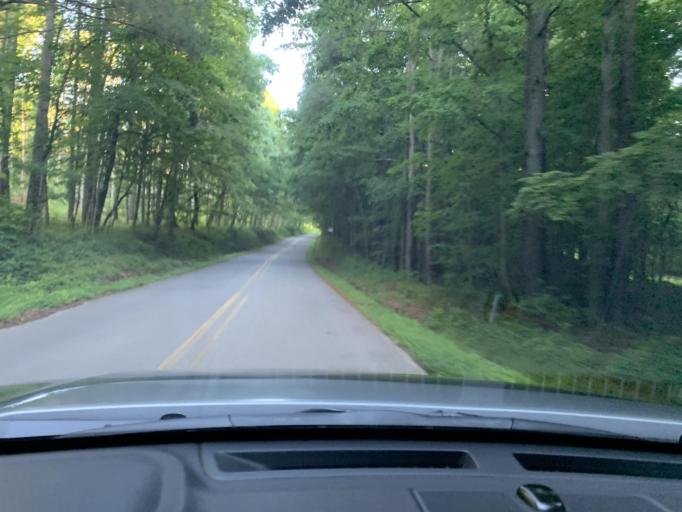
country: US
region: Georgia
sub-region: Bartow County
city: Rydal
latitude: 34.2345
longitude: -84.6642
